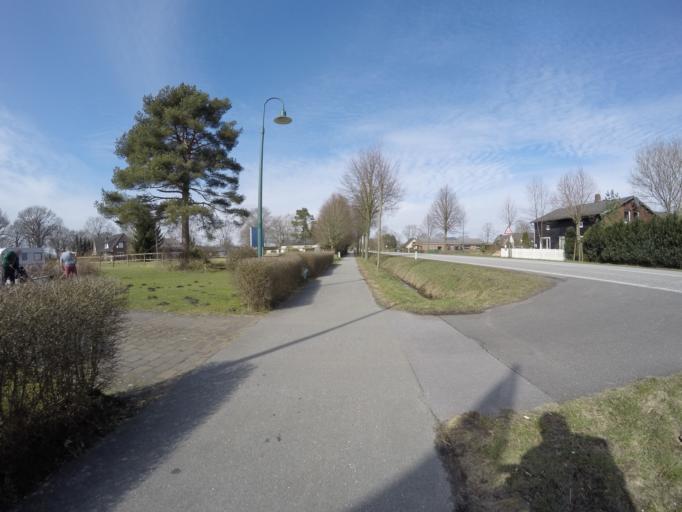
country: DE
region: Schleswig-Holstein
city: Bilsen
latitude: 53.7759
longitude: 9.8755
